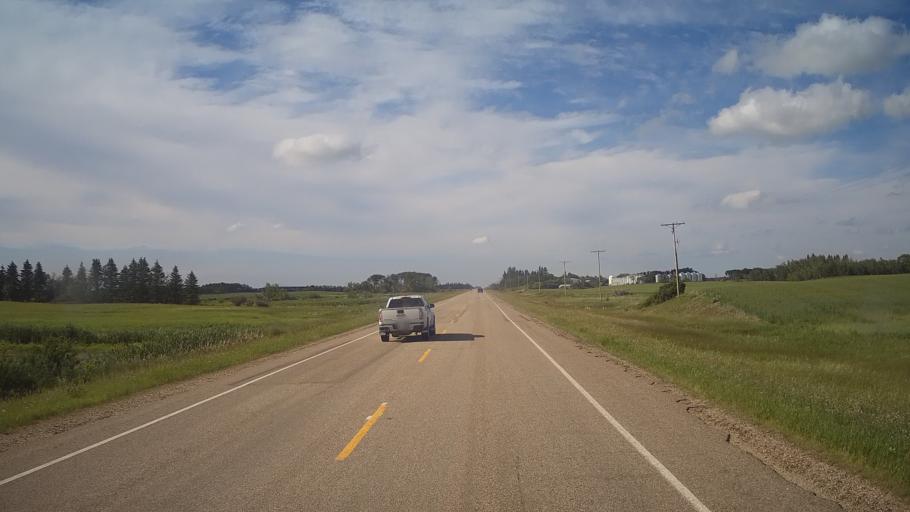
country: CA
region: Saskatchewan
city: Foam Lake
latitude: 51.5839
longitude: -103.8458
